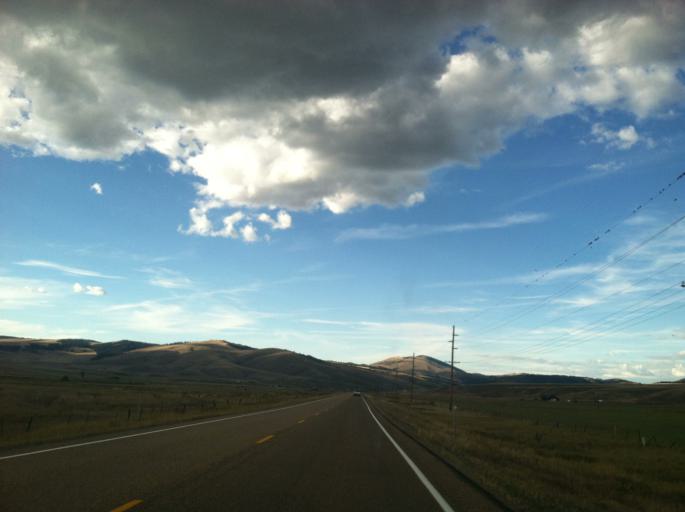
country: US
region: Montana
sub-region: Granite County
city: Philipsburg
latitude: 46.3442
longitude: -113.3124
